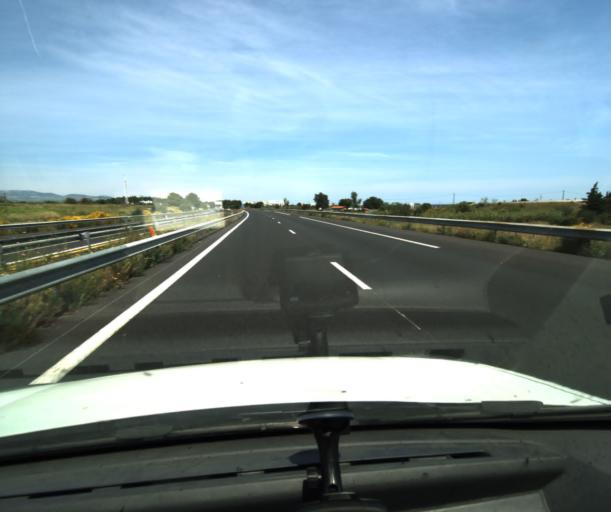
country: FR
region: Languedoc-Roussillon
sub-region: Departement des Pyrenees-Orientales
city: Pia
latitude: 42.7446
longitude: 2.8907
